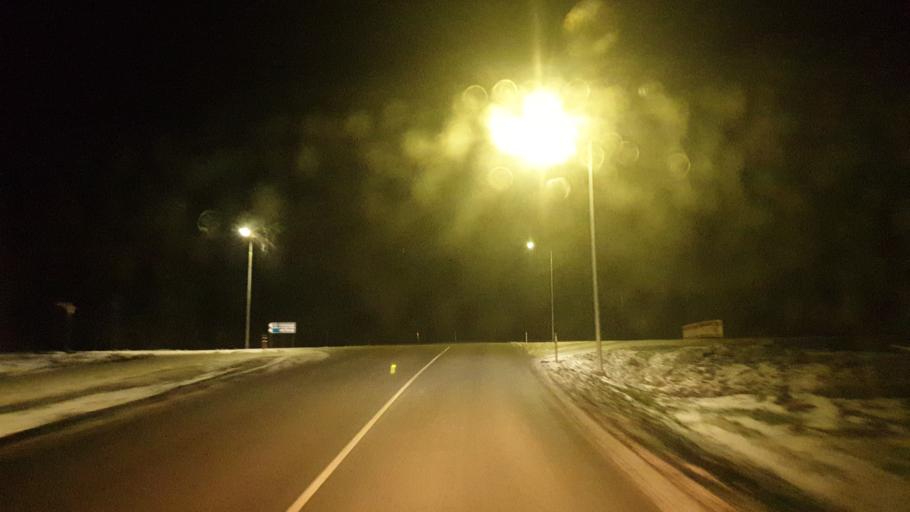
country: FI
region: Southern Savonia
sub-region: Pieksaemaeki
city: Juva
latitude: 61.8760
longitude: 27.7708
